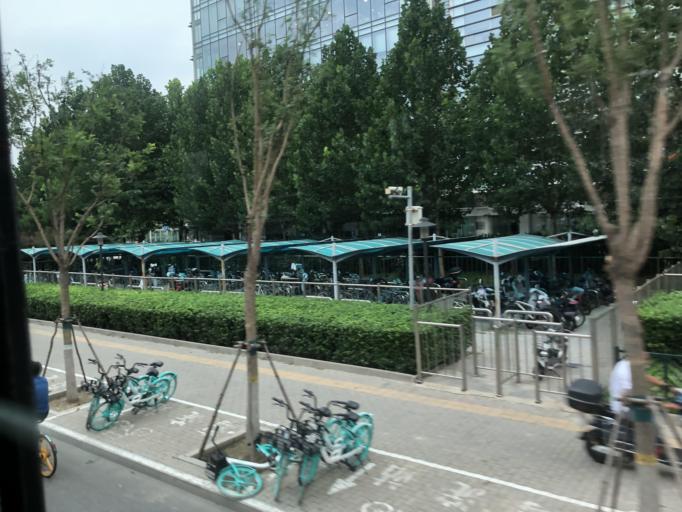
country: CN
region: Beijing
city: Jinrongjie
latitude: 39.9322
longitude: 116.3191
